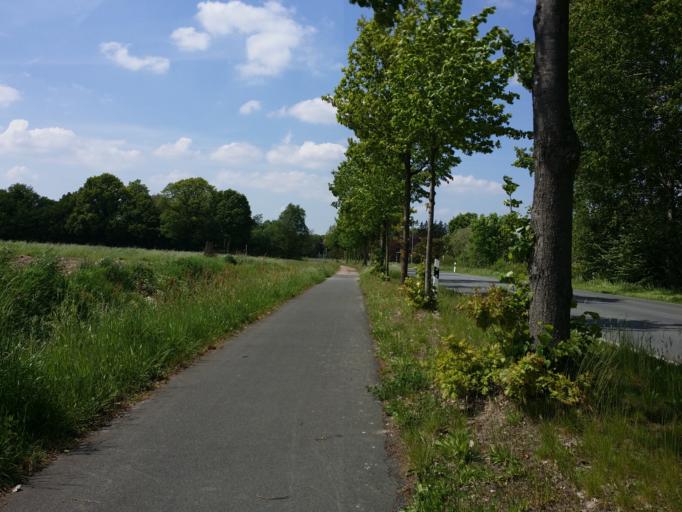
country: DE
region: Lower Saxony
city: Lubberstedt
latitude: 53.2992
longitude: 8.7628
